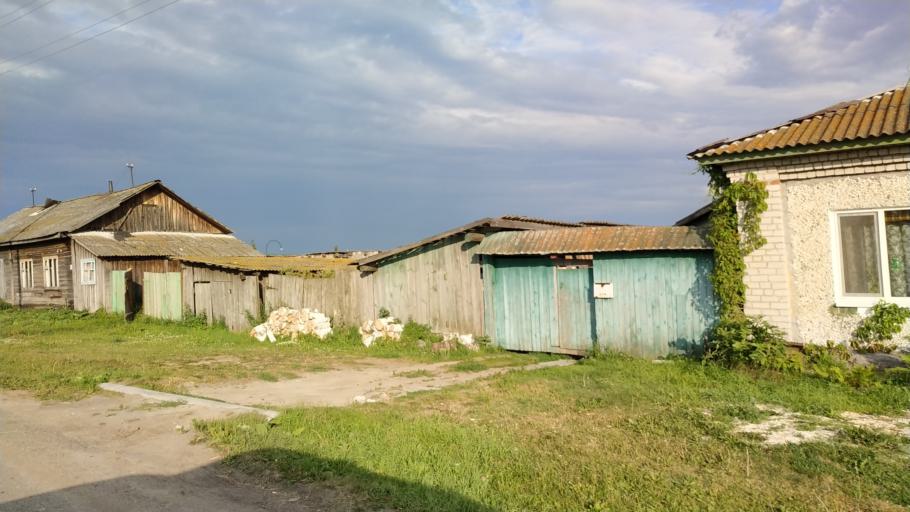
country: RU
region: Sverdlovsk
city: Yelanskiy
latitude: 57.0814
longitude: 62.4724
